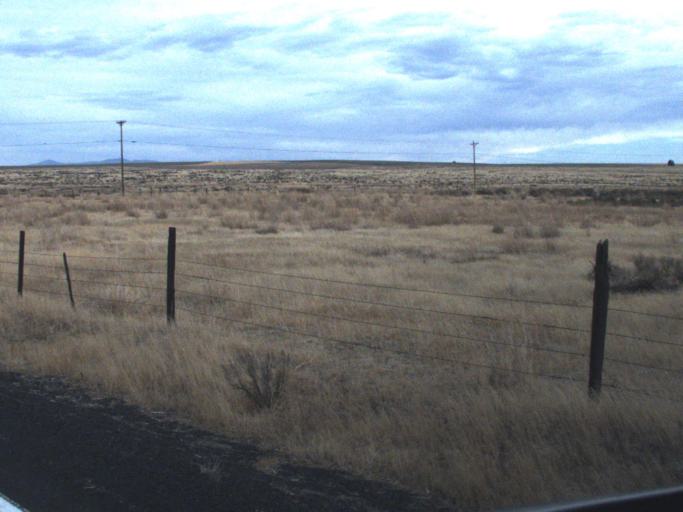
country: US
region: Washington
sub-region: Okanogan County
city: Coulee Dam
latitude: 47.6698
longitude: -118.7216
